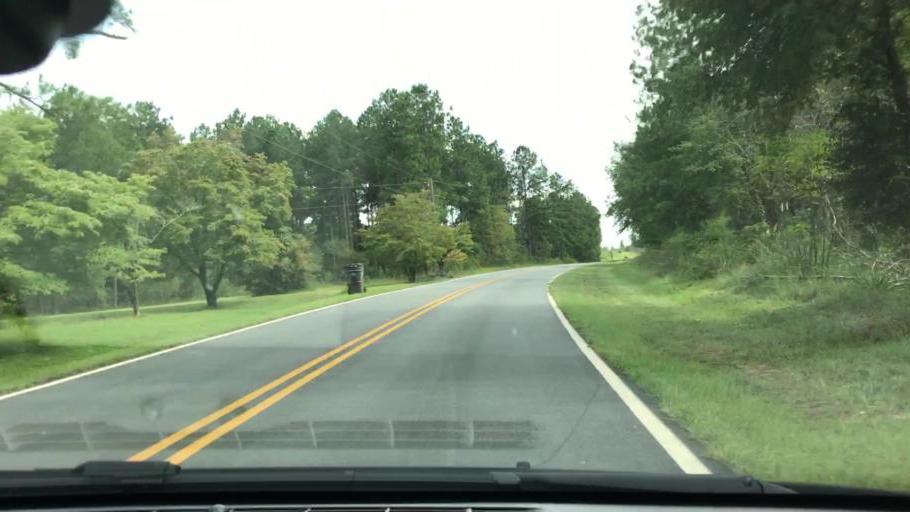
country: US
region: Georgia
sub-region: Clay County
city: Fort Gaines
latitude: 31.5487
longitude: -84.9661
